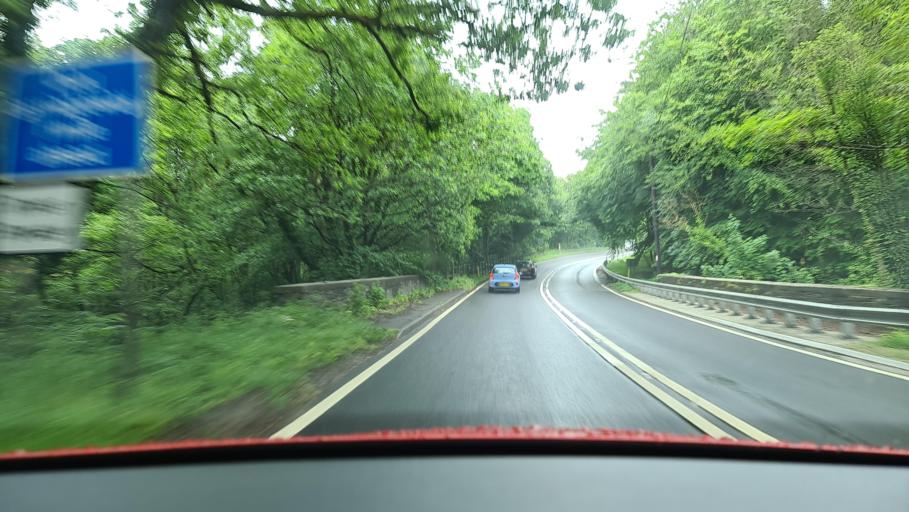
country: GB
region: England
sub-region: Cornwall
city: Liskeard
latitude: 50.4575
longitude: -4.5524
